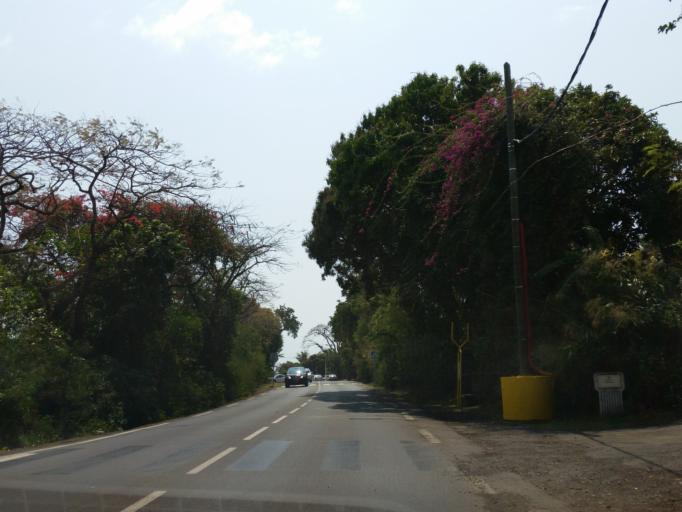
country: RE
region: Reunion
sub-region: Reunion
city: Sainte-Marie
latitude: -20.9038
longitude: 55.5071
